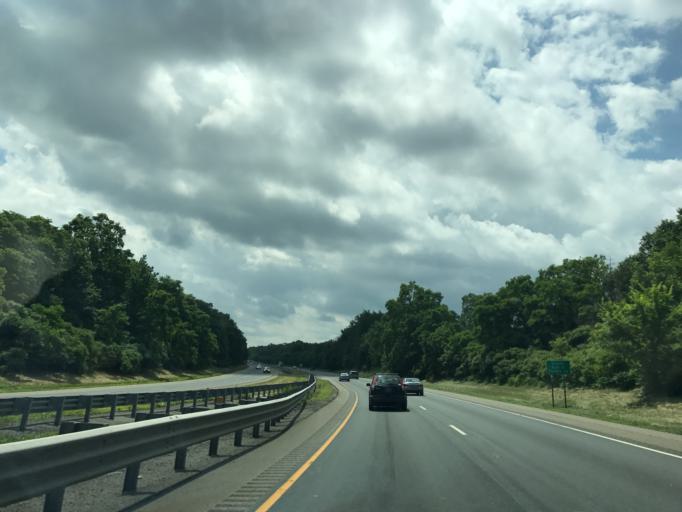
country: US
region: New Jersey
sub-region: Morris County
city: Madison
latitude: 40.7653
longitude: -74.4021
